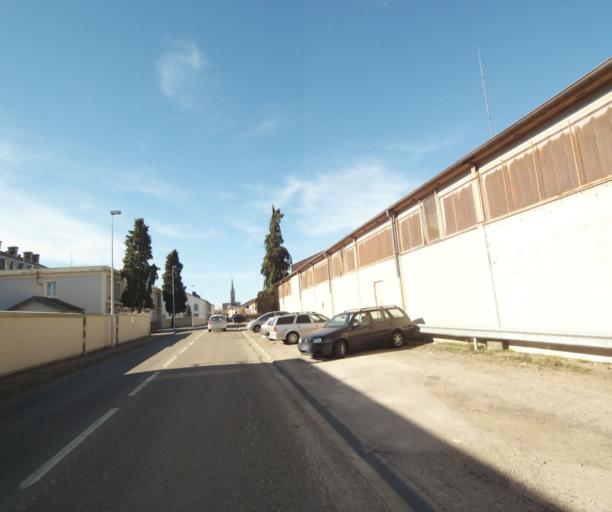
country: FR
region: Lorraine
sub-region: Departement de Meurthe-et-Moselle
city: Nancy
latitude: 48.6699
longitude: 6.1834
